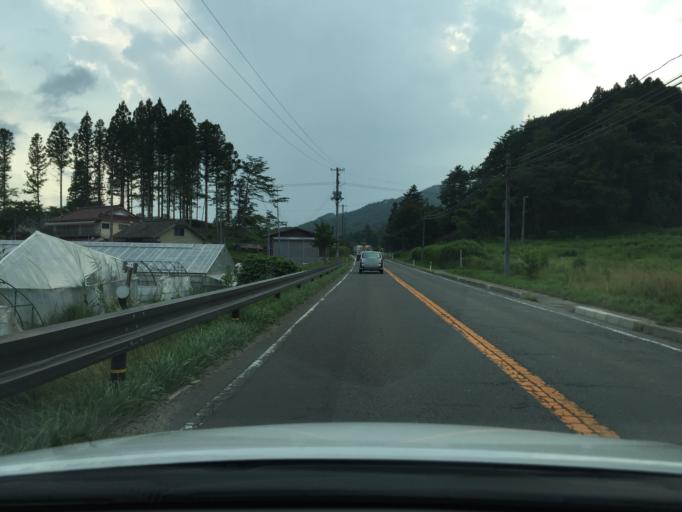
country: JP
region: Fukushima
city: Yanagawamachi-saiwaicho
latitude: 37.6960
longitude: 140.7240
